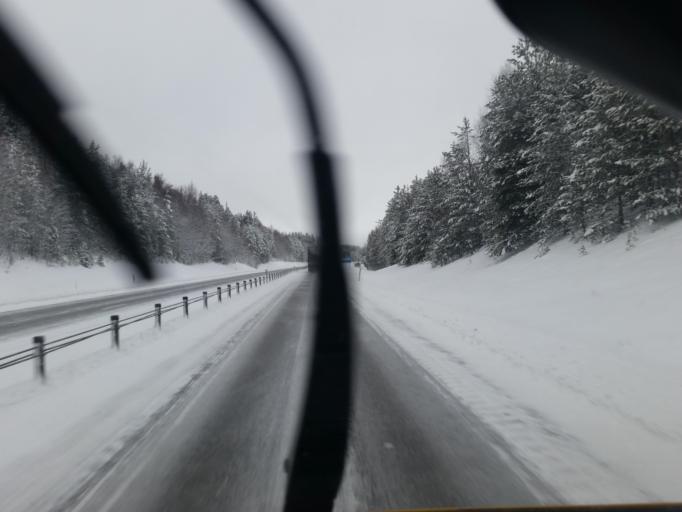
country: SE
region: Norrbotten
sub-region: Pitea Kommun
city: Bergsviken
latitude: 65.3010
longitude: 21.4149
